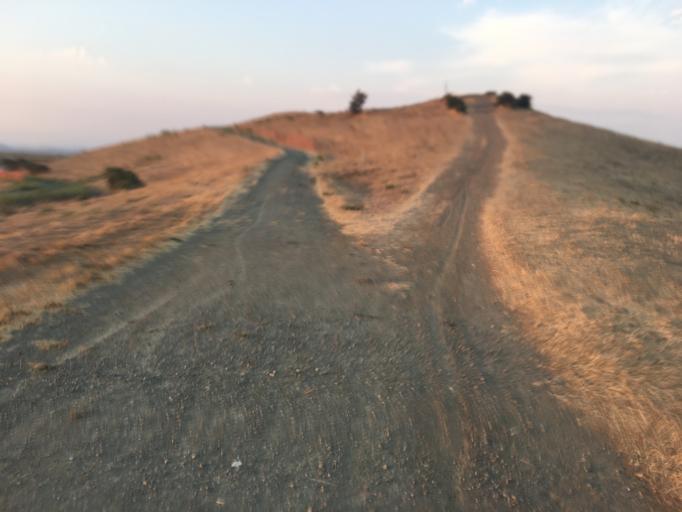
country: US
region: California
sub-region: Santa Clara County
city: Mountain View
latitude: 37.4265
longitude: -122.0742
